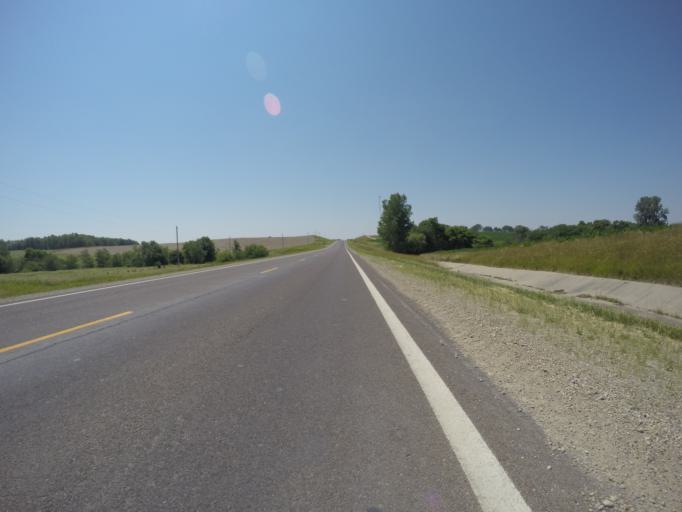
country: US
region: Kansas
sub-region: Doniphan County
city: Highland
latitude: 39.8535
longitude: -95.2651
